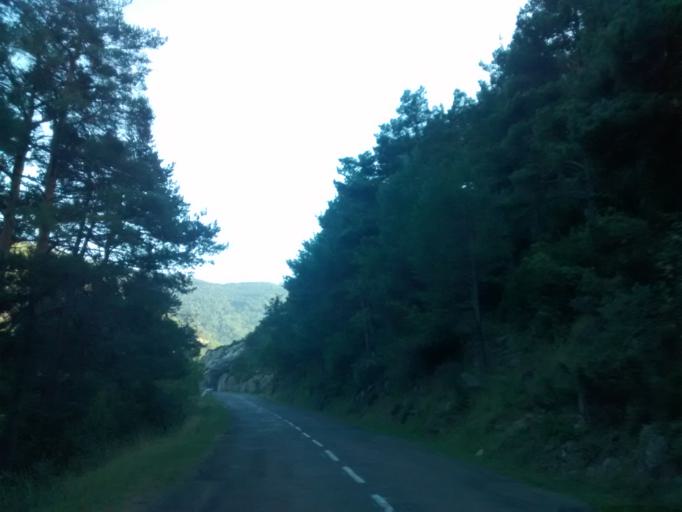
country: ES
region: Aragon
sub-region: Provincia de Huesca
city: Anso
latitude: 42.7879
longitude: -0.7374
